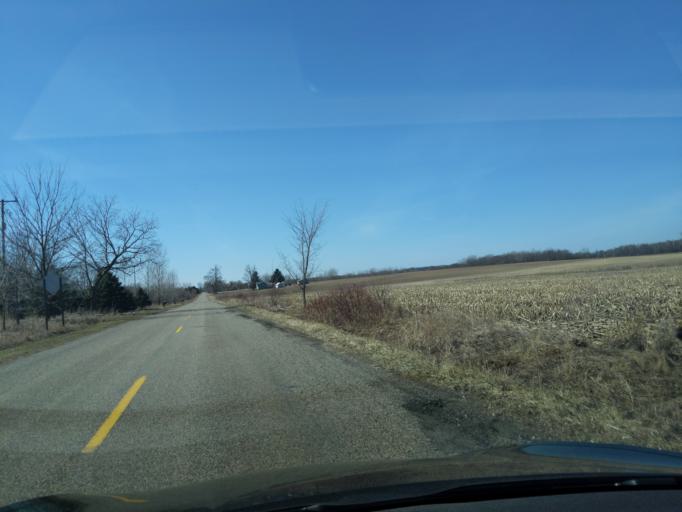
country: US
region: Michigan
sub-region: Ionia County
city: Portland
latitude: 42.7267
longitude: -84.9577
